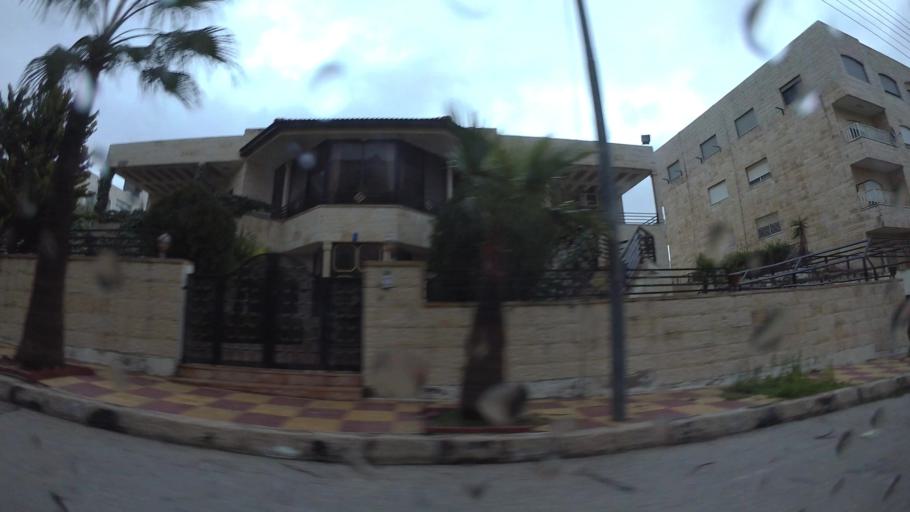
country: JO
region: Amman
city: Amman
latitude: 31.9985
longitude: 35.9284
